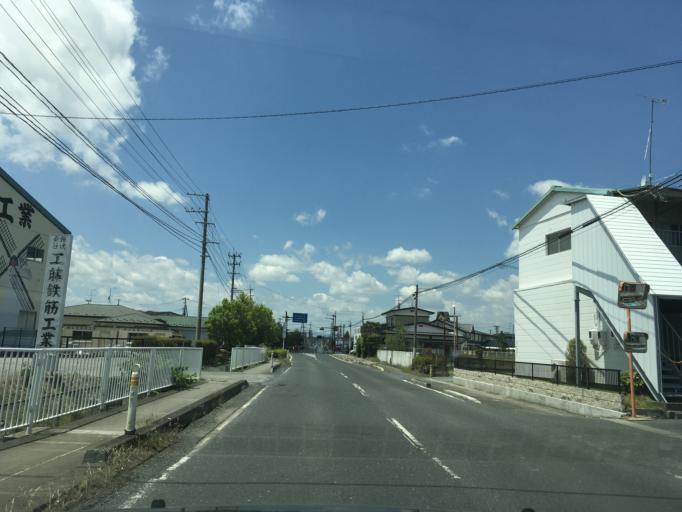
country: JP
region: Miyagi
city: Wakuya
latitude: 38.6817
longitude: 141.2100
